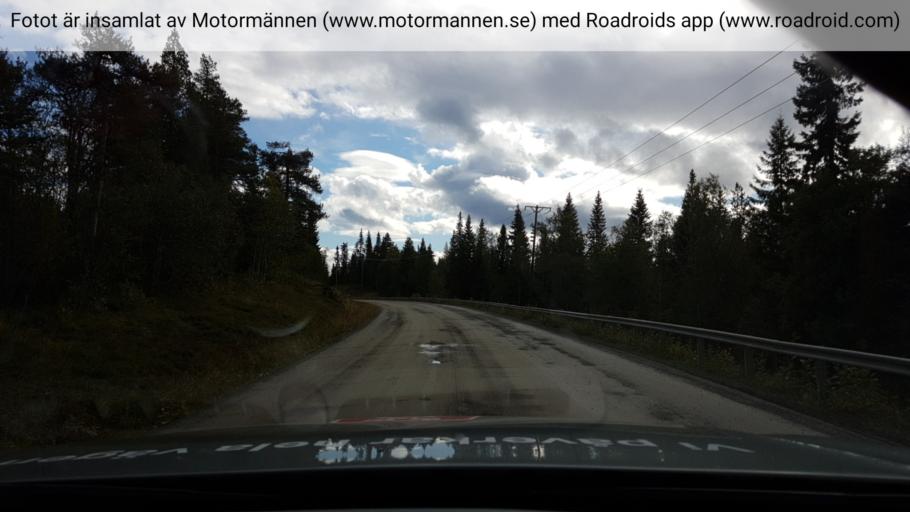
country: SE
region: Jaemtland
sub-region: Are Kommun
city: Are
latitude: 63.6797
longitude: 12.8126
